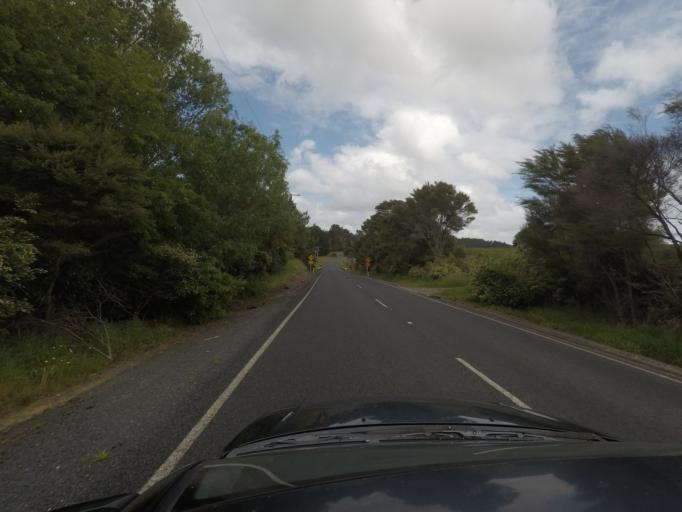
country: NZ
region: Auckland
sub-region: Auckland
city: Parakai
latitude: -36.6551
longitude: 174.5230
